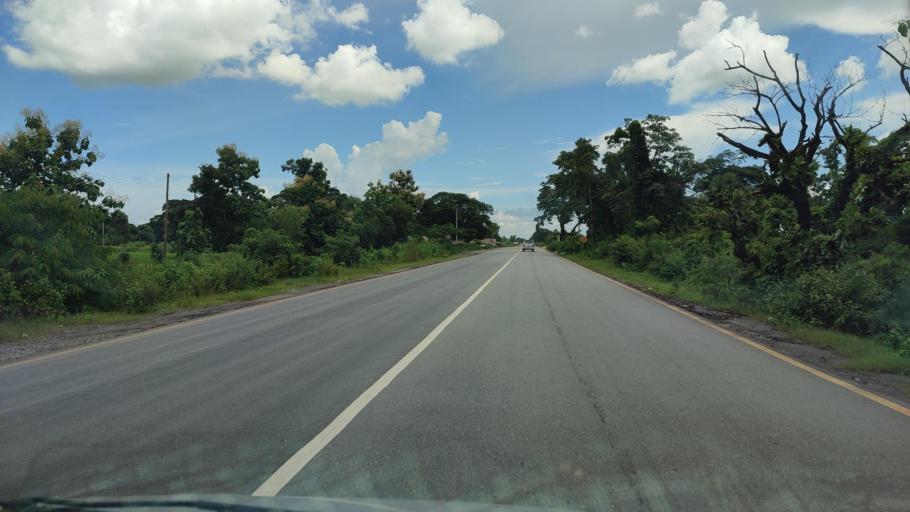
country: MM
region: Bago
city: Nyaunglebin
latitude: 17.9997
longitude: 96.7031
